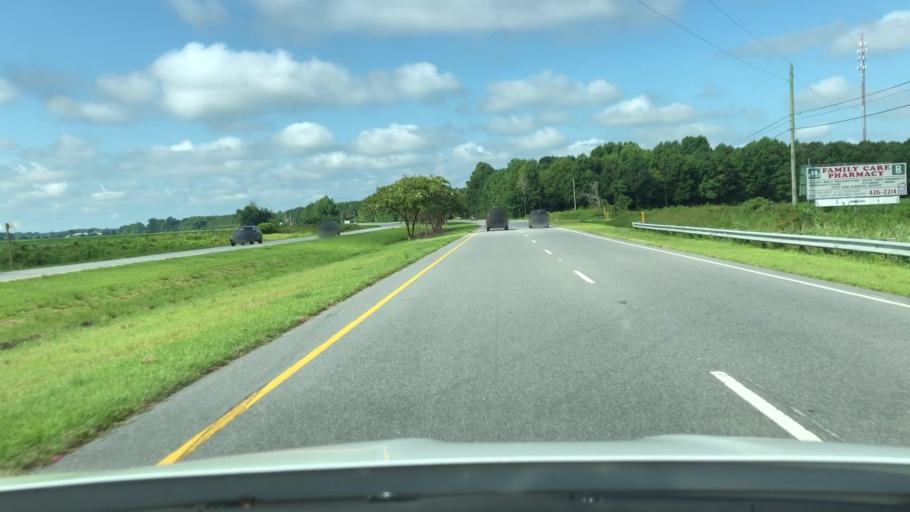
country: US
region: North Carolina
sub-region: Perquimans County
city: Hertford
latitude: 36.2087
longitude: -76.4424
